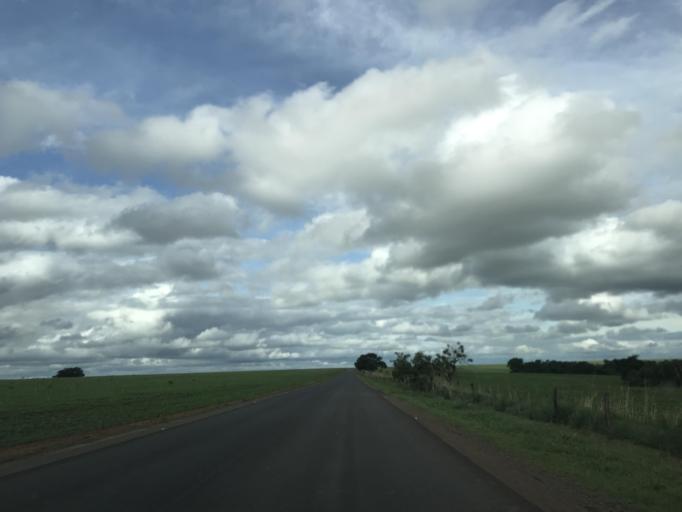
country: BR
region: Goias
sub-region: Vianopolis
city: Vianopolis
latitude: -16.9653
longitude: -48.6464
